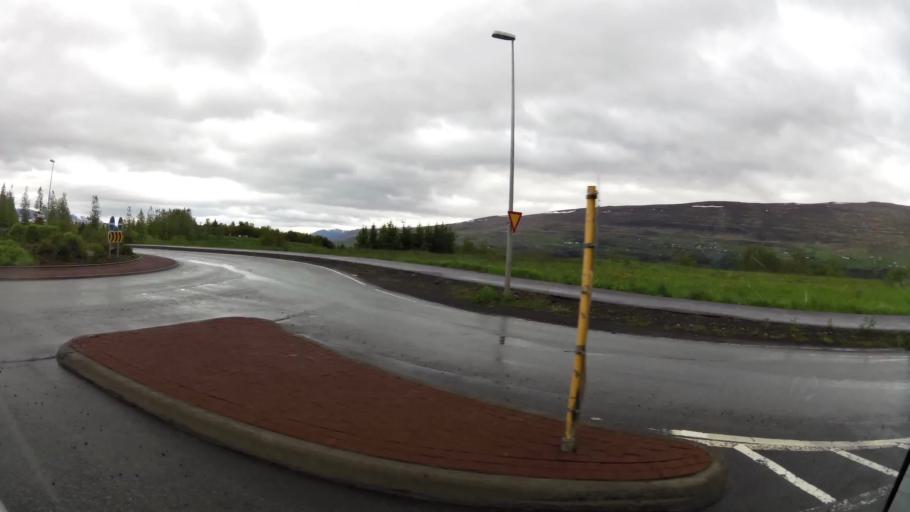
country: IS
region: Northeast
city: Akureyri
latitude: 65.6647
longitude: -18.0894
